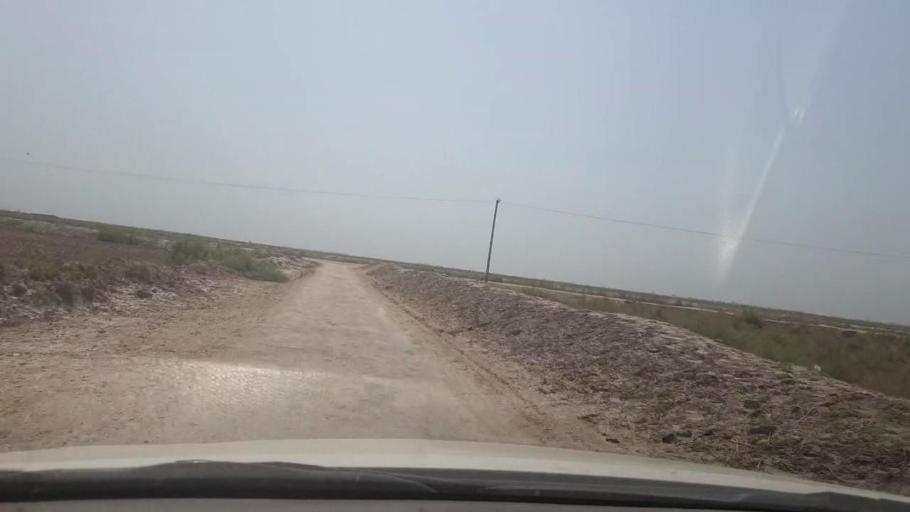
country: PK
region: Sindh
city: Garhi Yasin
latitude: 27.9867
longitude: 68.5028
